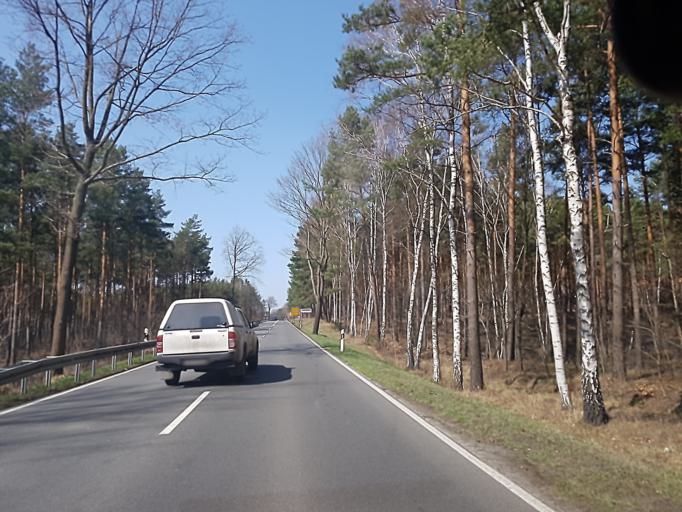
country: DE
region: Brandenburg
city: Tschernitz
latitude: 51.6275
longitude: 14.5788
